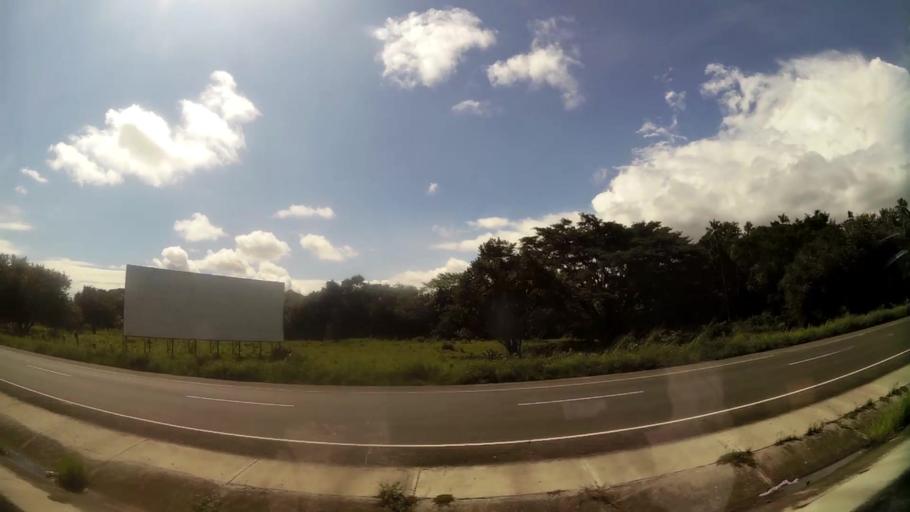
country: PA
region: Panama
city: Bejuco
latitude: 8.6283
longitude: -79.8810
